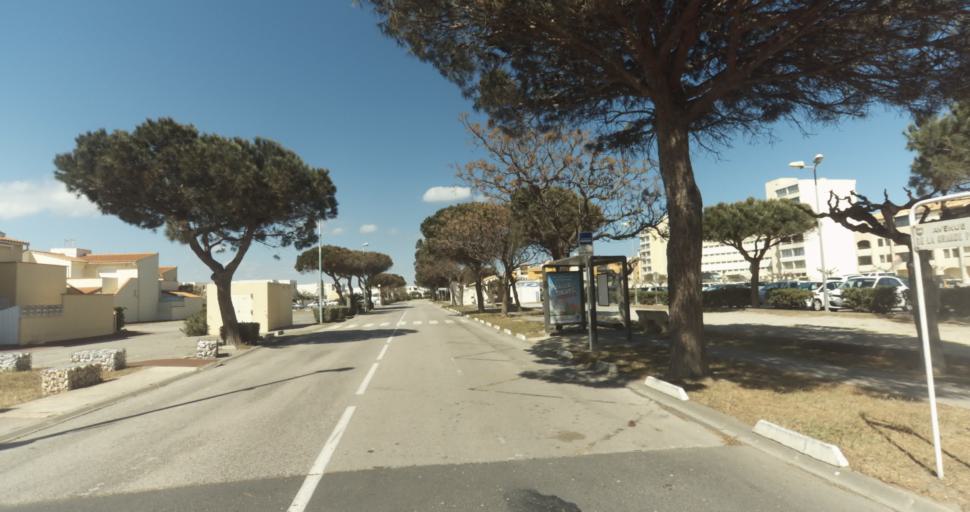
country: FR
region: Languedoc-Roussillon
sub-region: Departement des Pyrenees-Orientales
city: Le Barcares
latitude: 42.8342
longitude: 3.0398
